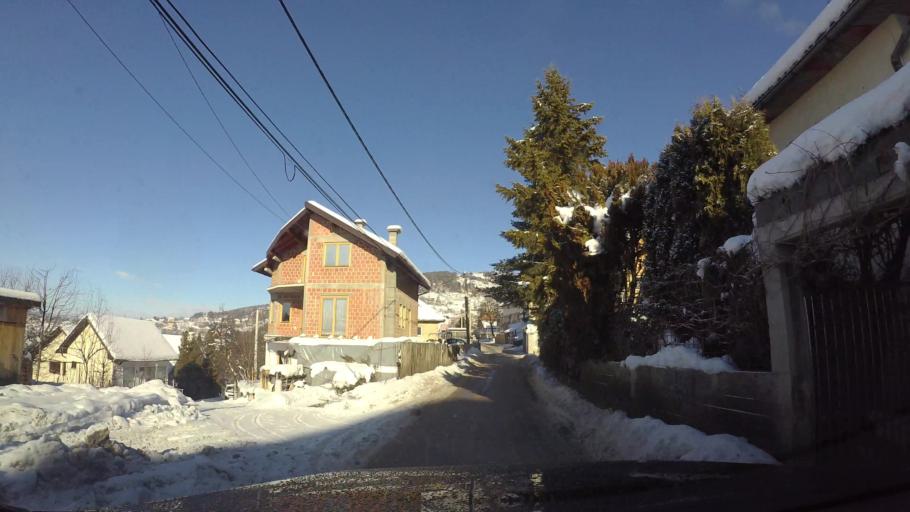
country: BA
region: Federation of Bosnia and Herzegovina
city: Kobilja Glava
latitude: 43.8902
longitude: 18.4089
